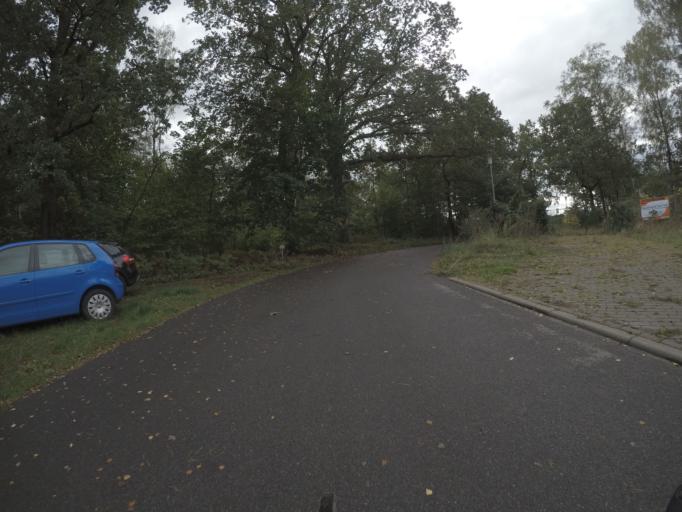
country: DE
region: Berlin
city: Buch
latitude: 52.6817
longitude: 13.4737
